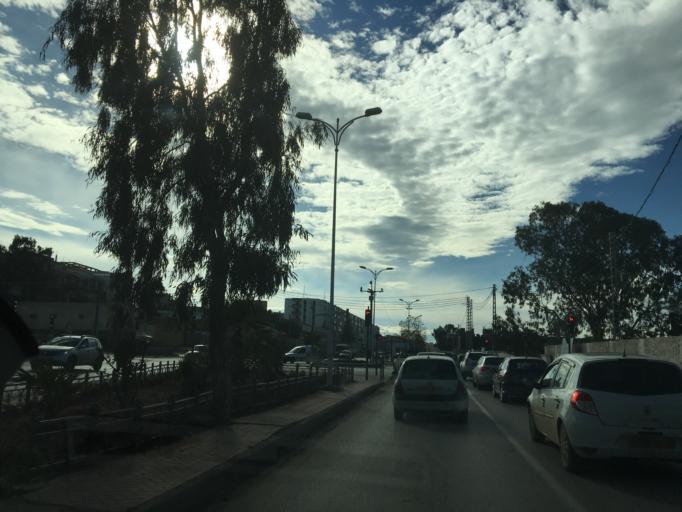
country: DZ
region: Alger
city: Bordj el Kiffan
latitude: 36.7617
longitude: 3.2326
